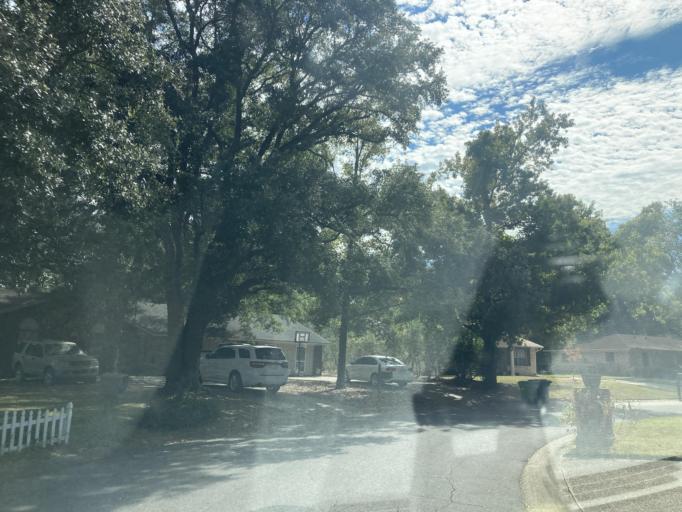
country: US
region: Mississippi
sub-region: Jackson County
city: Saint Martin
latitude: 30.4496
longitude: -88.8773
